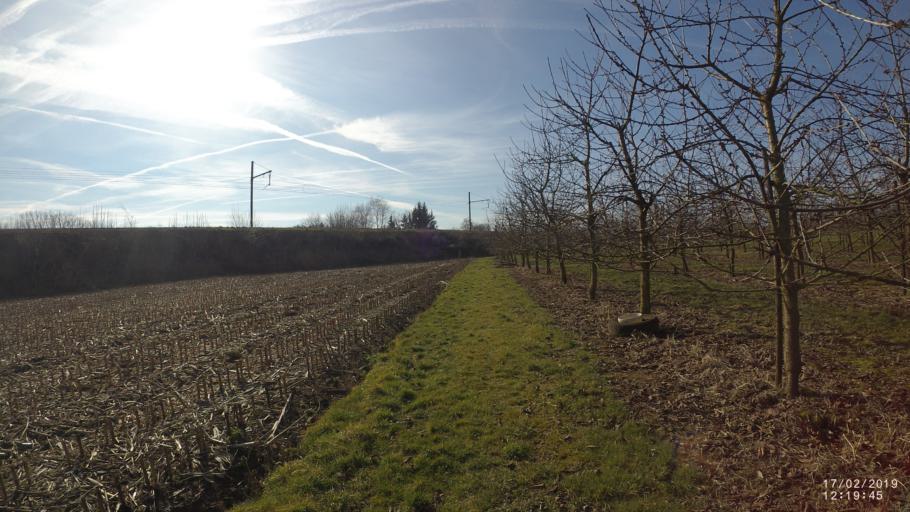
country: BE
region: Flanders
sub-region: Provincie Limburg
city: Sint-Truiden
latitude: 50.8105
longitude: 5.1537
